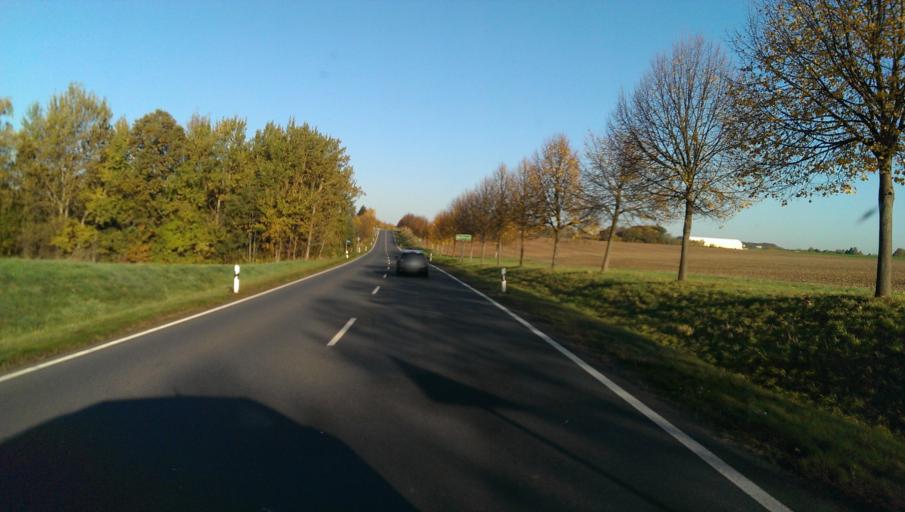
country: DE
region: Saxony
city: Niederwiesa
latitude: 50.8935
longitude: 12.9852
